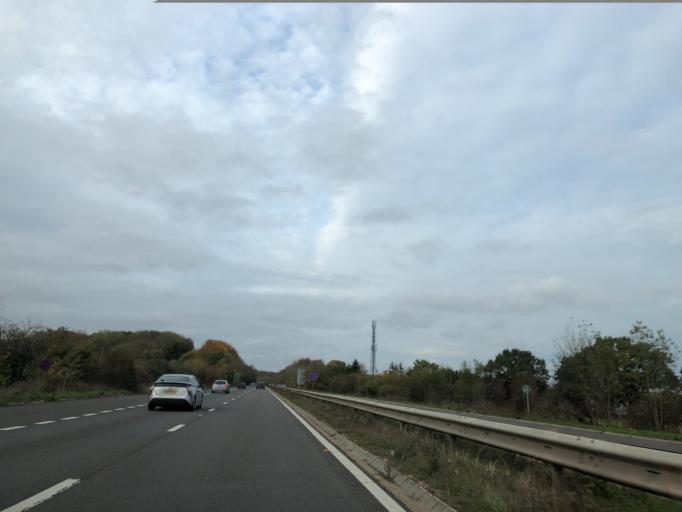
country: GB
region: England
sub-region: Buckinghamshire
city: Marlow
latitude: 51.5834
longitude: -0.7573
